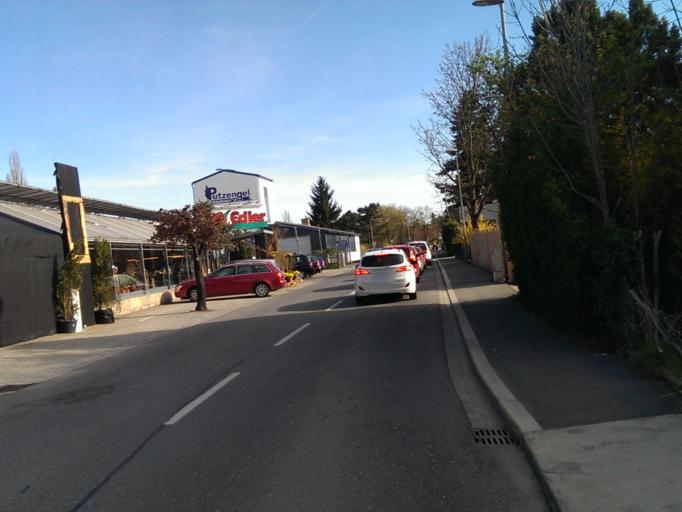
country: AT
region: Styria
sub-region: Politischer Bezirk Graz-Umgebung
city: Feldkirchen bei Graz
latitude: 47.0408
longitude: 15.4567
